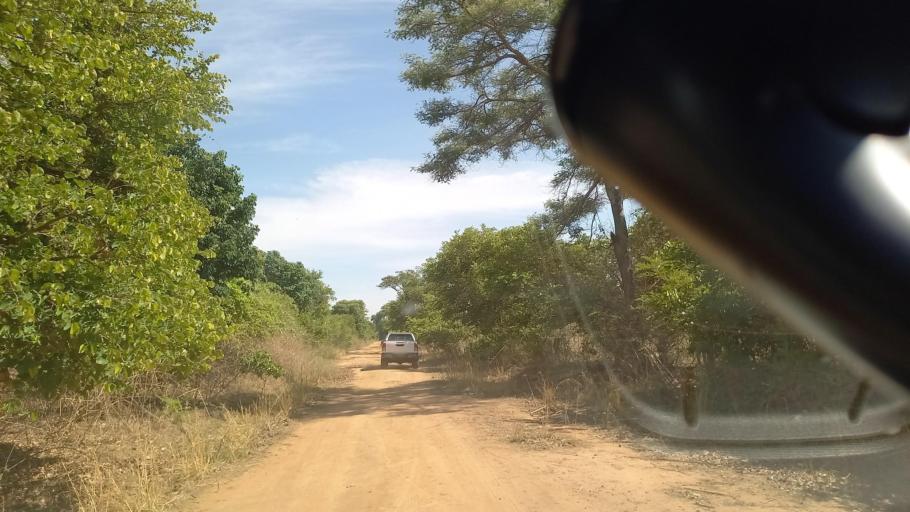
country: ZM
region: Southern
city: Mazabuka
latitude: -16.0395
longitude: 27.6220
